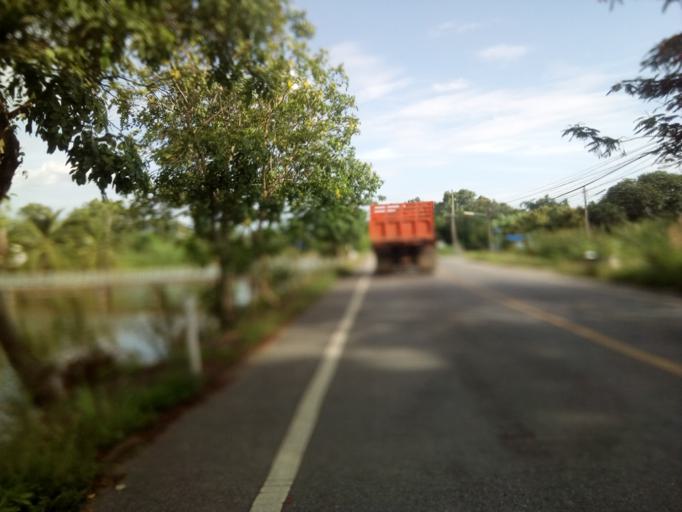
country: TH
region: Pathum Thani
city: Nong Suea
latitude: 14.1479
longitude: 100.8459
